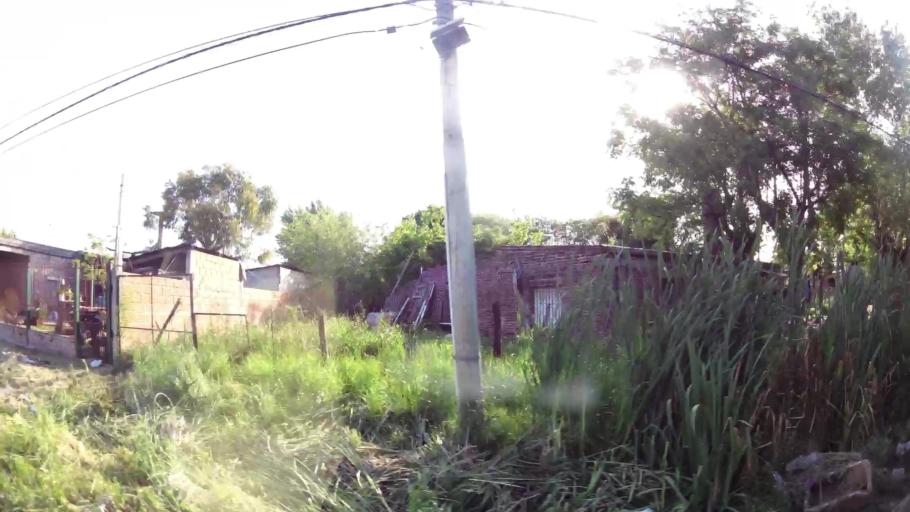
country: AR
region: Buenos Aires
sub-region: Partido de Almirante Brown
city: Adrogue
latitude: -34.8133
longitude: -58.3305
